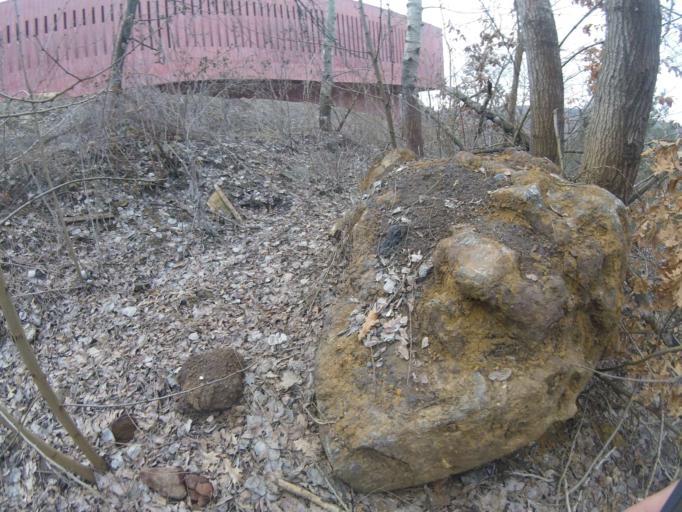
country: HU
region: Borsod-Abauj-Zemplen
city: Rudabanya
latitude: 48.3947
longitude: 20.6445
